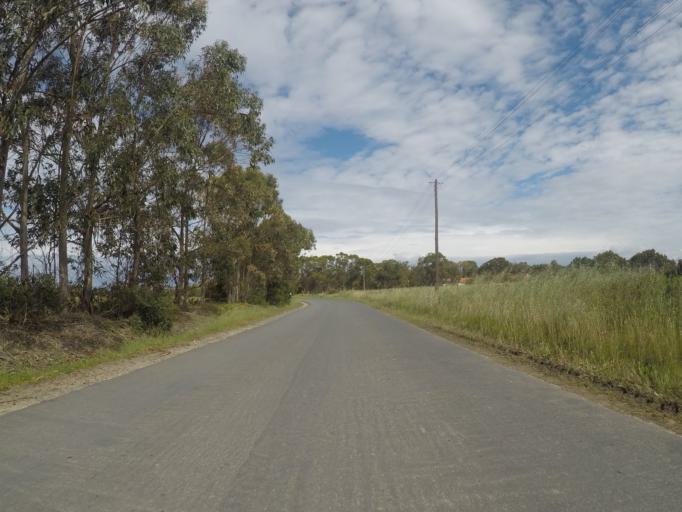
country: PT
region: Beja
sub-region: Odemira
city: Sao Teotonio
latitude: 37.4939
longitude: -8.7844
